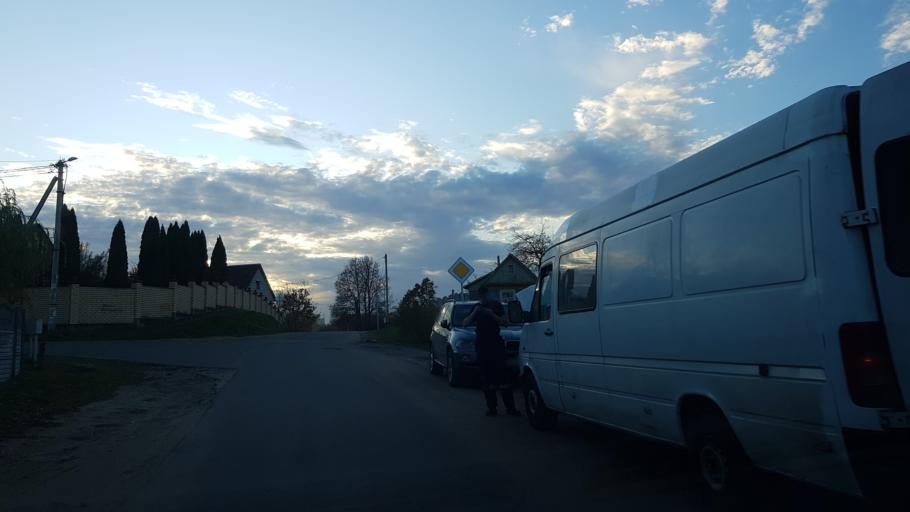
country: BY
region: Minsk
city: Vyaliki Trastsyanets
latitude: 53.8520
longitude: 27.7145
